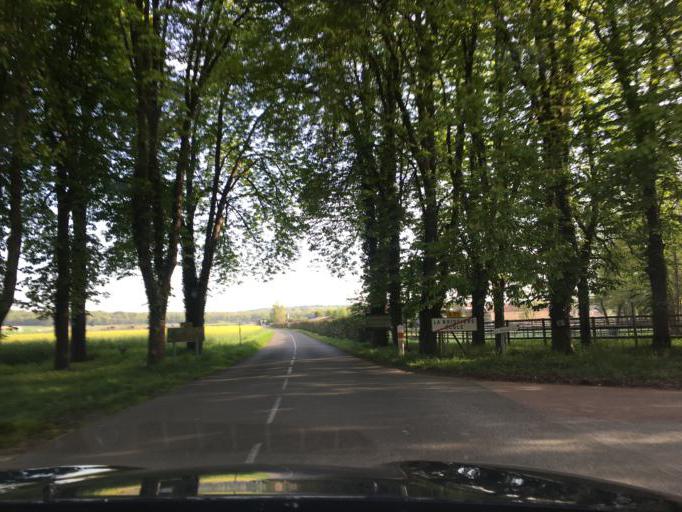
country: FR
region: Ile-de-France
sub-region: Departement des Yvelines
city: Conde-sur-Vesgre
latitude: 48.6831
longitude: 1.6545
